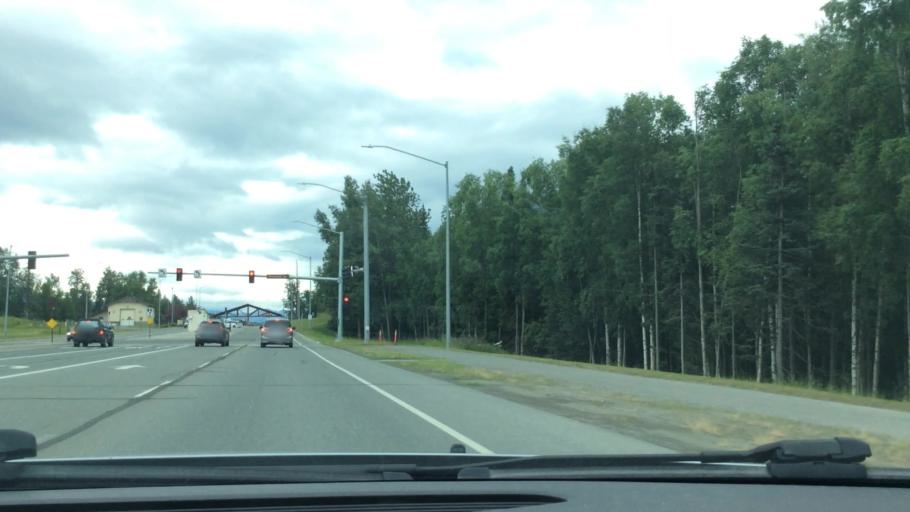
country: US
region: Alaska
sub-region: Anchorage Municipality
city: Anchorage
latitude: 61.2340
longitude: -149.7787
